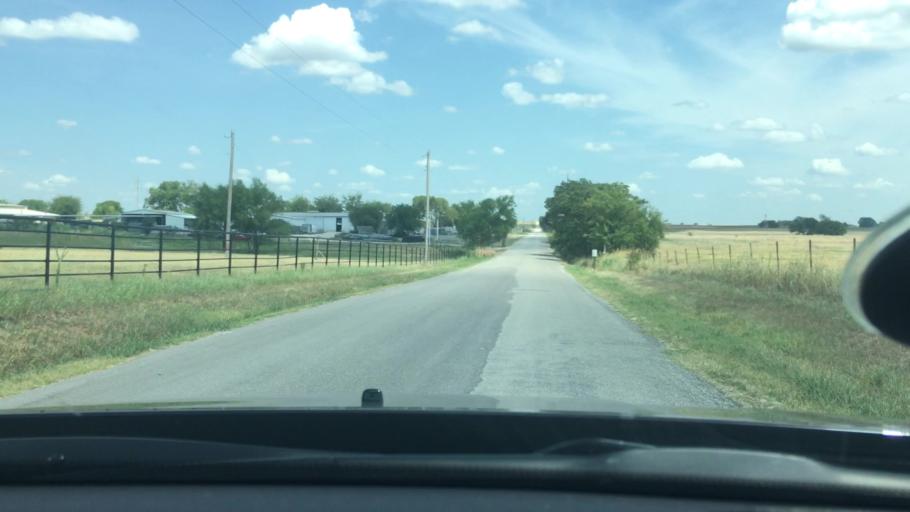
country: US
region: Oklahoma
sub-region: Love County
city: Marietta
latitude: 33.9451
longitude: -97.1869
